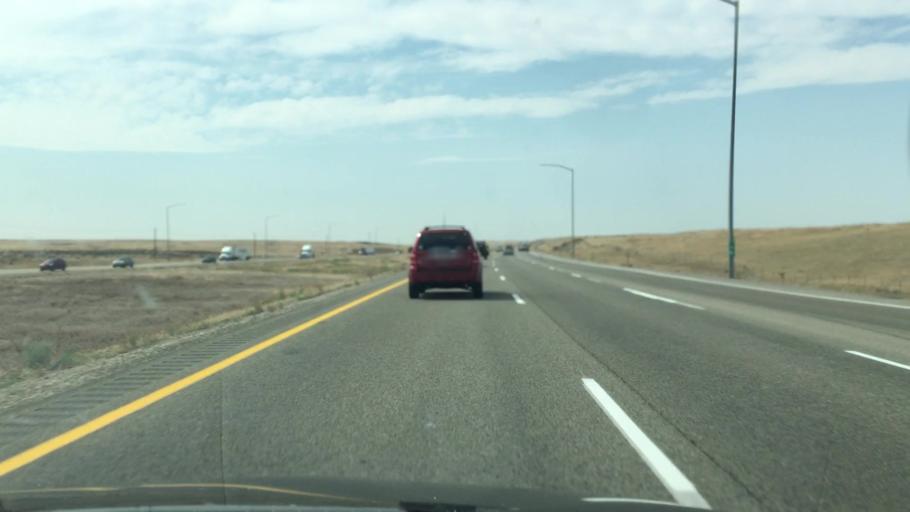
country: US
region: Idaho
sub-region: Ada County
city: Boise
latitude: 43.4347
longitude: -116.0612
